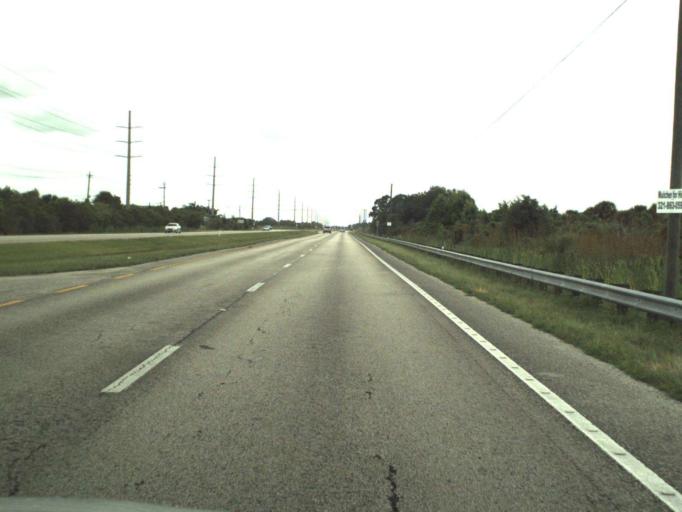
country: US
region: Florida
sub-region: Brevard County
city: Titusville
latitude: 28.5507
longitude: -80.8573
